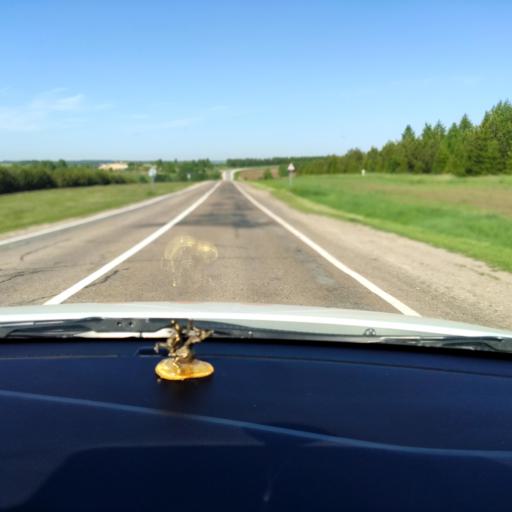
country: RU
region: Tatarstan
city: Vysokaya Gora
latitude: 56.0176
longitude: 49.2771
